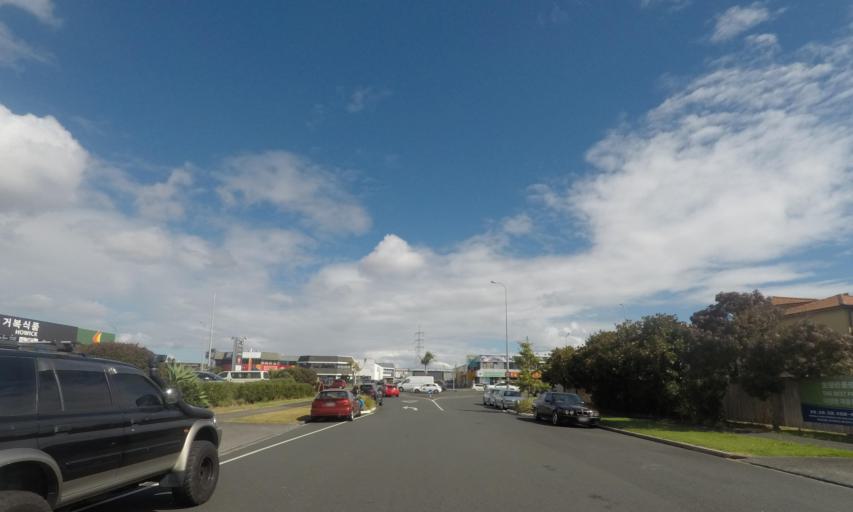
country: NZ
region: Auckland
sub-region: Auckland
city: Pakuranga
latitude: -36.9263
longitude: 174.8972
